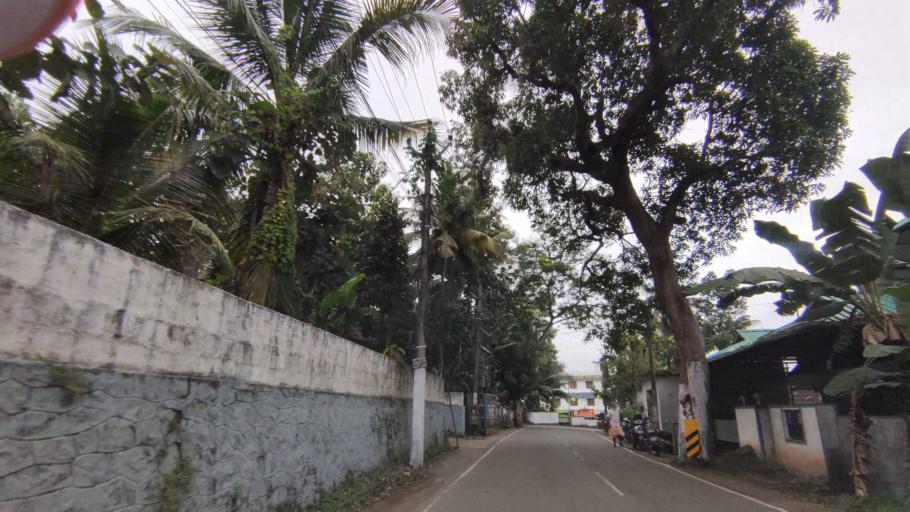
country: IN
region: Kerala
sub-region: Kottayam
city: Kottayam
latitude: 9.6499
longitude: 76.5210
